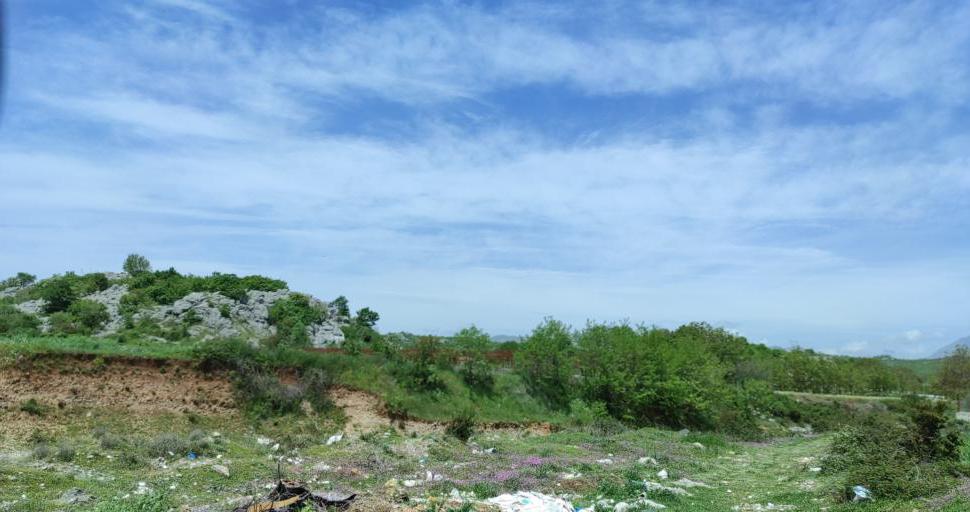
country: AL
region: Shkoder
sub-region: Rrethi i Malesia e Madhe
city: Gruemire
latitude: 42.1501
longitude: 19.5352
